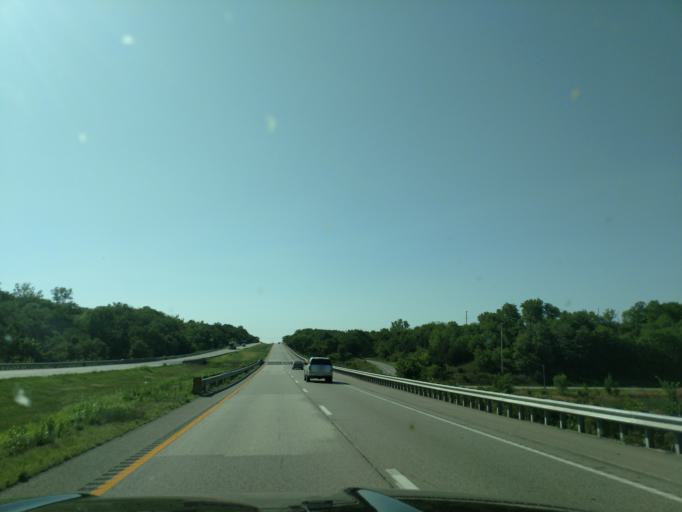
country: US
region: Missouri
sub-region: Andrew County
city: Savannah
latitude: 39.9031
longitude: -94.8835
